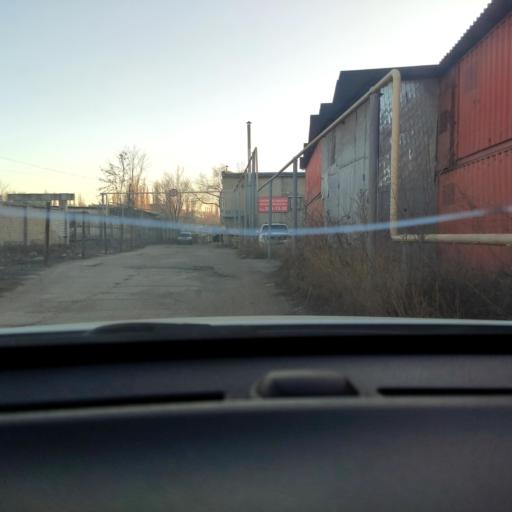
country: RU
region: Voronezj
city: Maslovka
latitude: 51.6132
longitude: 39.2422
